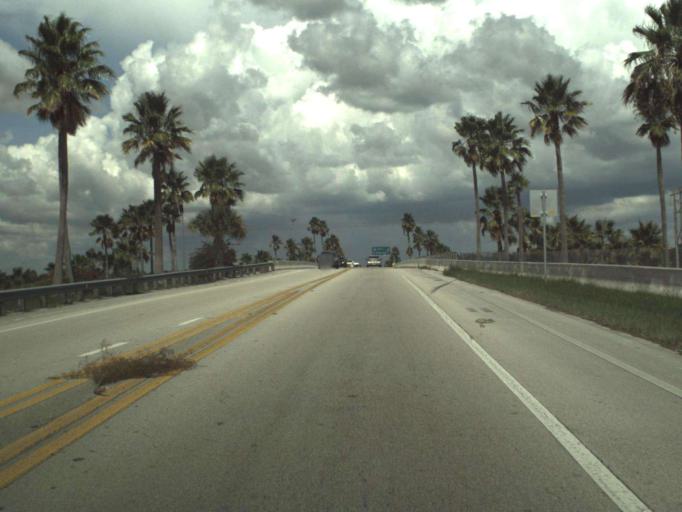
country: US
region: Florida
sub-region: Saint Lucie County
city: Port Saint Lucie
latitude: 27.3115
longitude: -80.4127
